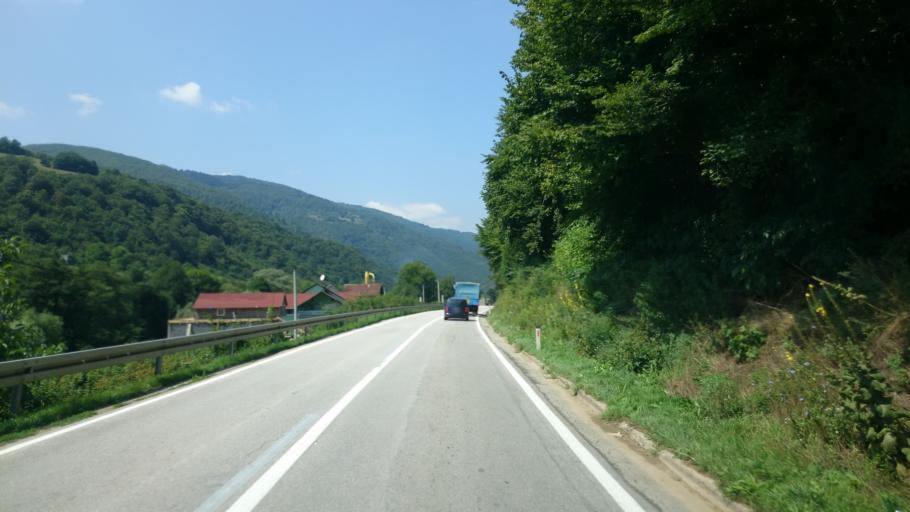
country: BA
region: Federation of Bosnia and Herzegovina
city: Donji Vakuf
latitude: 44.1747
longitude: 17.3583
